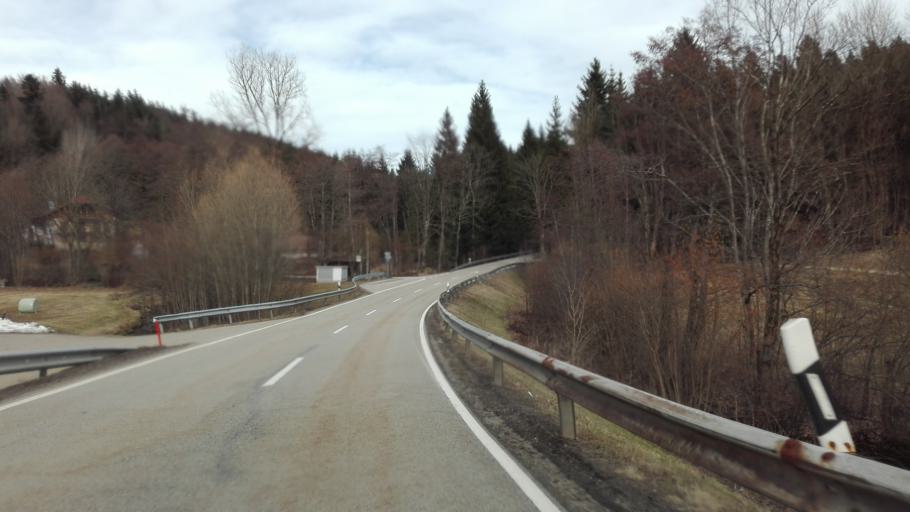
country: DE
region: Bavaria
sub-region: Lower Bavaria
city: Untergriesbach
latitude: 48.6085
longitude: 13.7056
